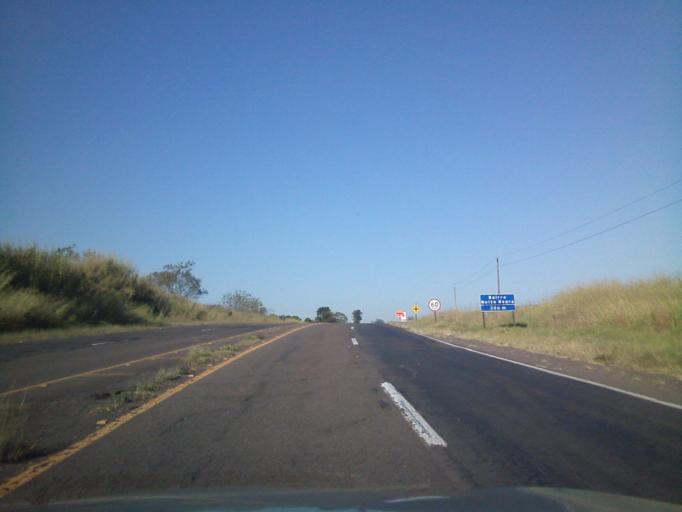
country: BR
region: Sao Paulo
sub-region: Presidente Prudente
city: Presidente Prudente
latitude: -22.2069
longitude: -51.4351
